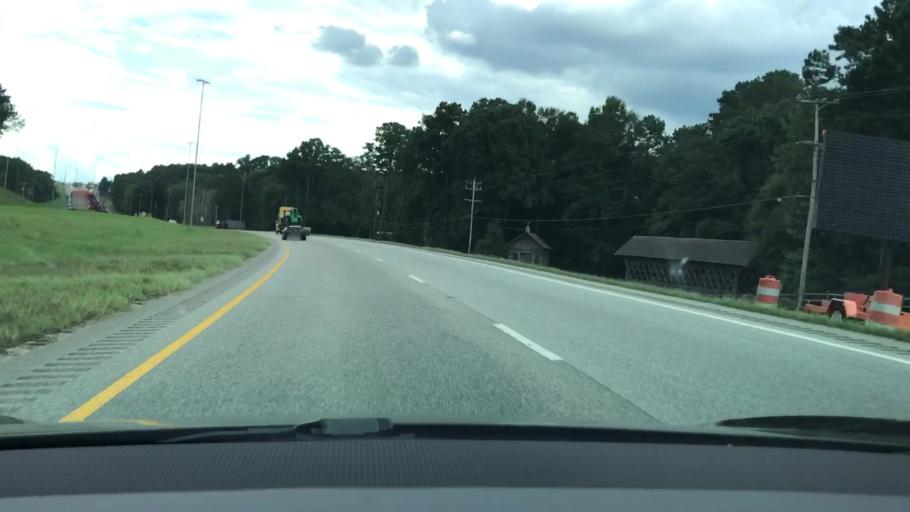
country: US
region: Alabama
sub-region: Pike County
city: Troy
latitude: 31.8240
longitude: -85.9951
